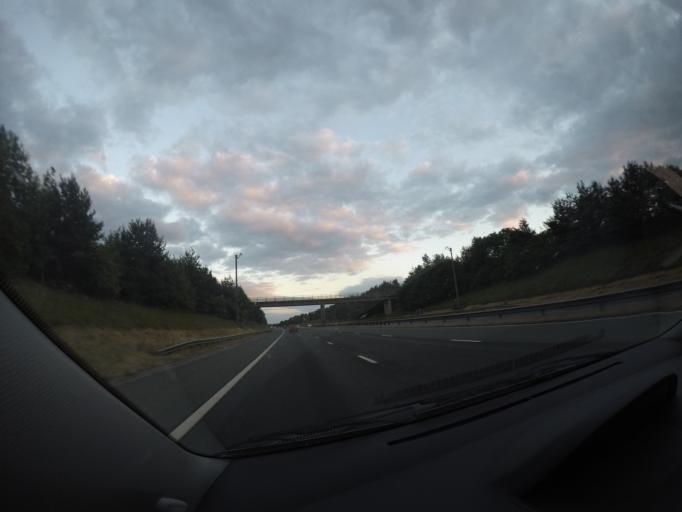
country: GB
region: England
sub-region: North Yorkshire
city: Boroughbridge
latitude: 54.1102
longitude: -1.4147
